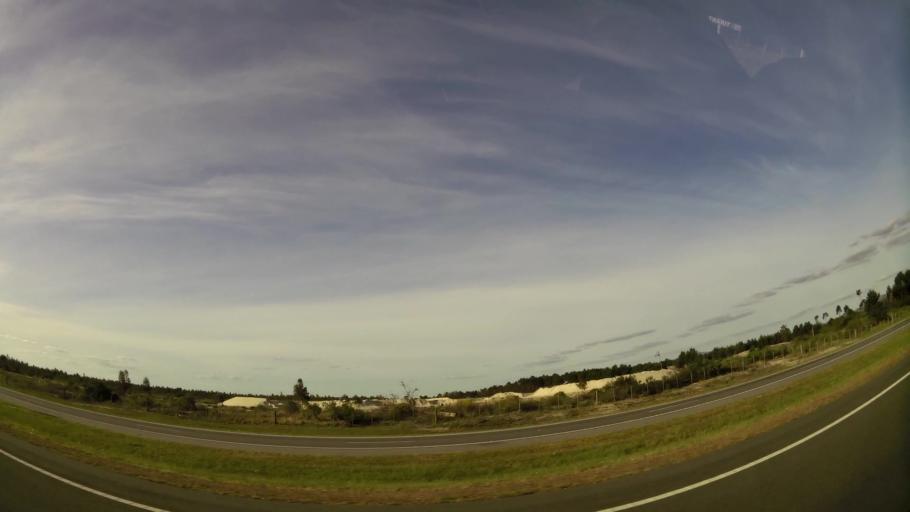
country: UY
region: Lavalleja
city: Solis de Mataojo
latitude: -34.7790
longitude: -55.4399
